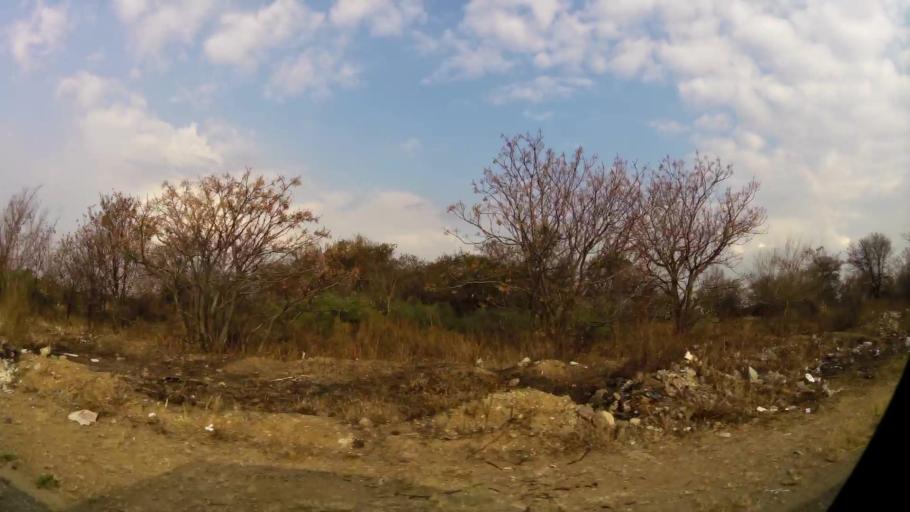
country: ZA
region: Gauteng
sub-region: Sedibeng District Municipality
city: Vereeniging
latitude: -26.6921
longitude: 27.8971
